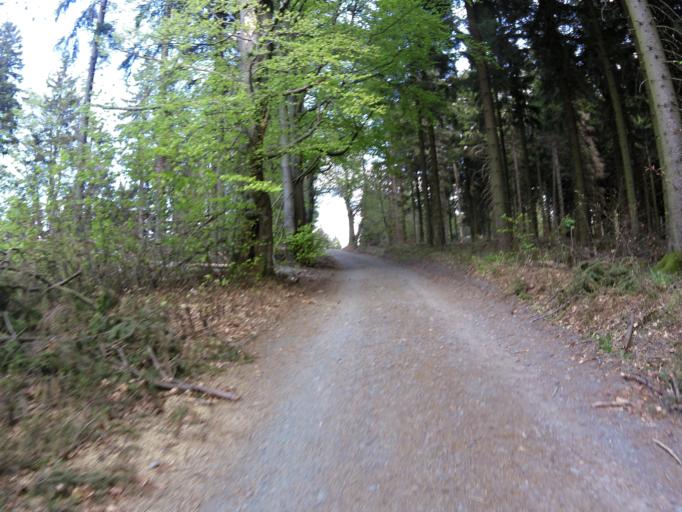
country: DE
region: Thuringia
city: Finsterbergen
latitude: 50.7840
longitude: 10.5432
